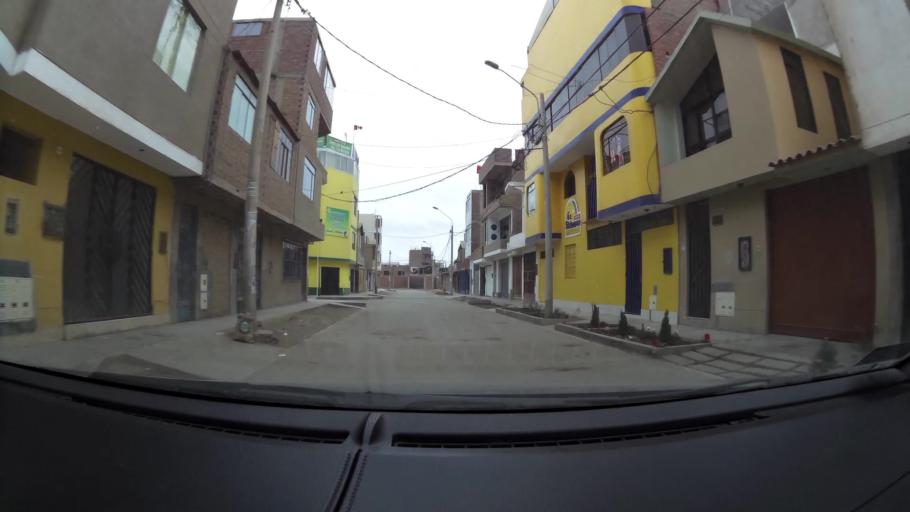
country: PE
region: Lima
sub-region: Lima
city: Independencia
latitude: -11.9733
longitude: -77.0924
